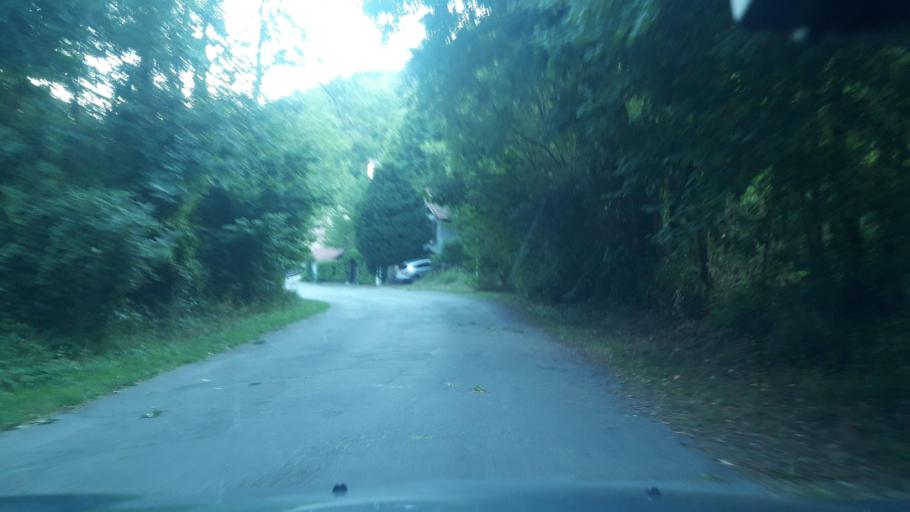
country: FR
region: Rhone-Alpes
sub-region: Departement de l'Isere
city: Biviers
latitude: 45.2367
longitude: 5.8006
